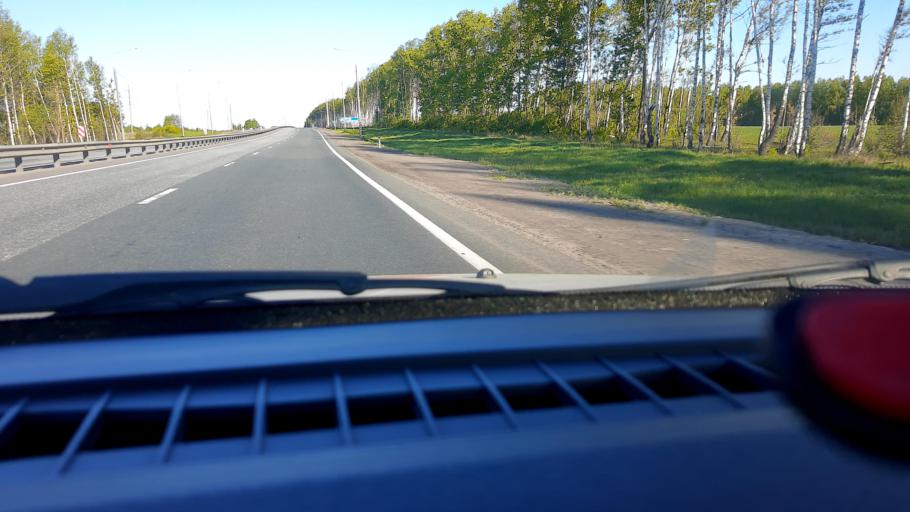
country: RU
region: Vladimir
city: Gorokhovets
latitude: 56.1593
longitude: 42.5168
